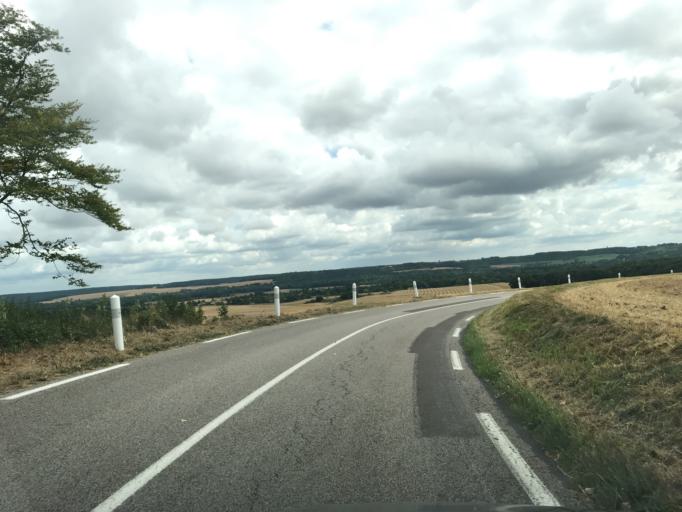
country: FR
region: Haute-Normandie
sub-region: Departement de l'Eure
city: Menilles
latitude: 49.0386
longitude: 1.2898
